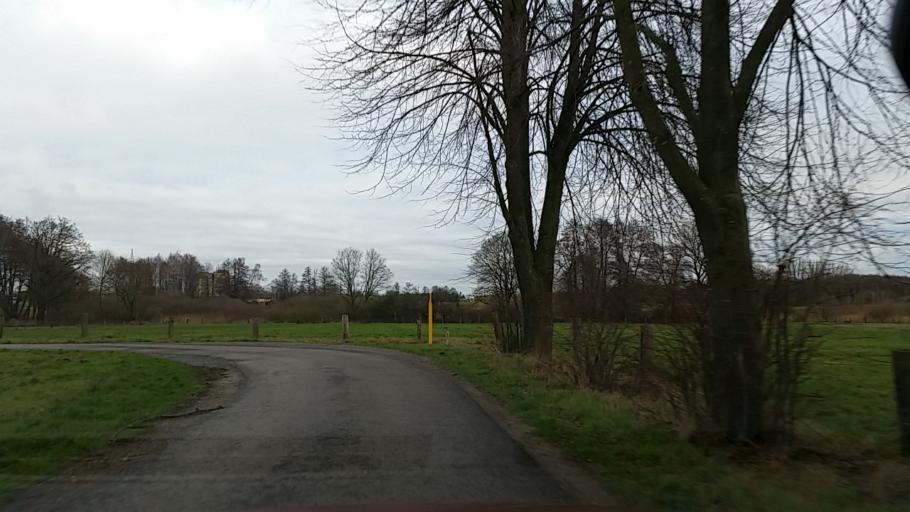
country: DE
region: Lower Saxony
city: Wittingen
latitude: 52.7144
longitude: 10.7292
